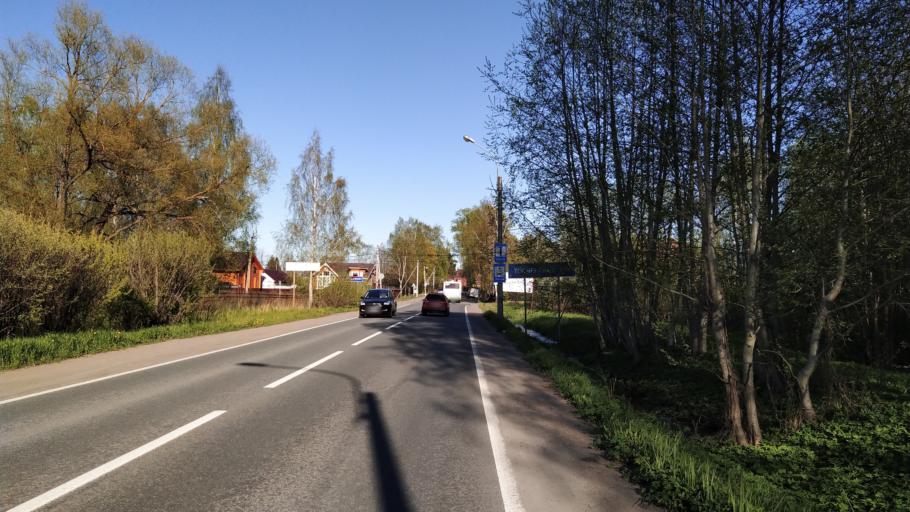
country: RU
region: St.-Petersburg
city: Tyarlevo
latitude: 59.6851
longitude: 30.4840
